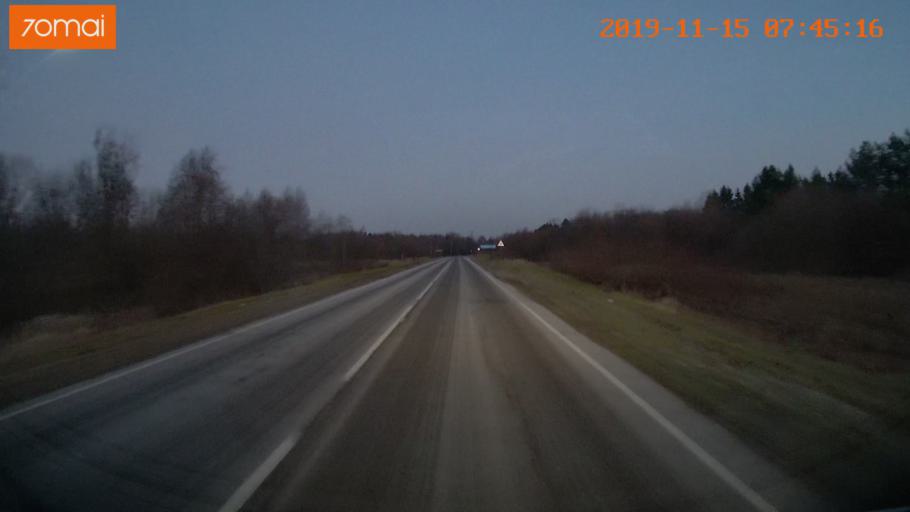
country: RU
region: Vologda
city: Sheksna
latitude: 58.8205
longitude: 38.3030
